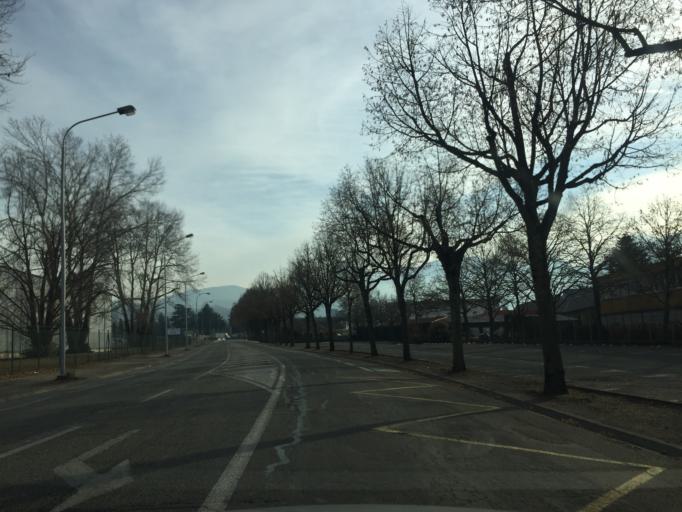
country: FR
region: Rhone-Alpes
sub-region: Departement de la Savoie
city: Cognin
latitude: 45.5811
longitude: 5.9031
